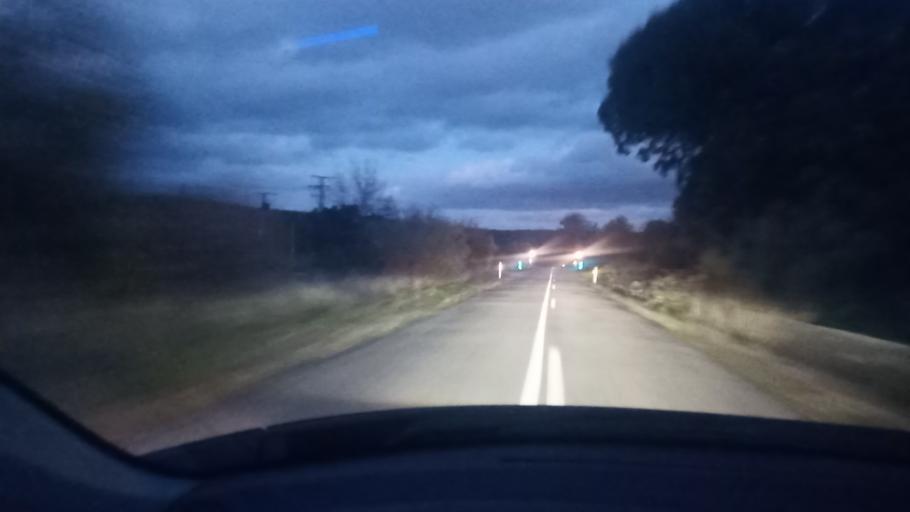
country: ES
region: Madrid
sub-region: Provincia de Madrid
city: Colmenar del Arroyo
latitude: 40.4295
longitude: -4.2188
